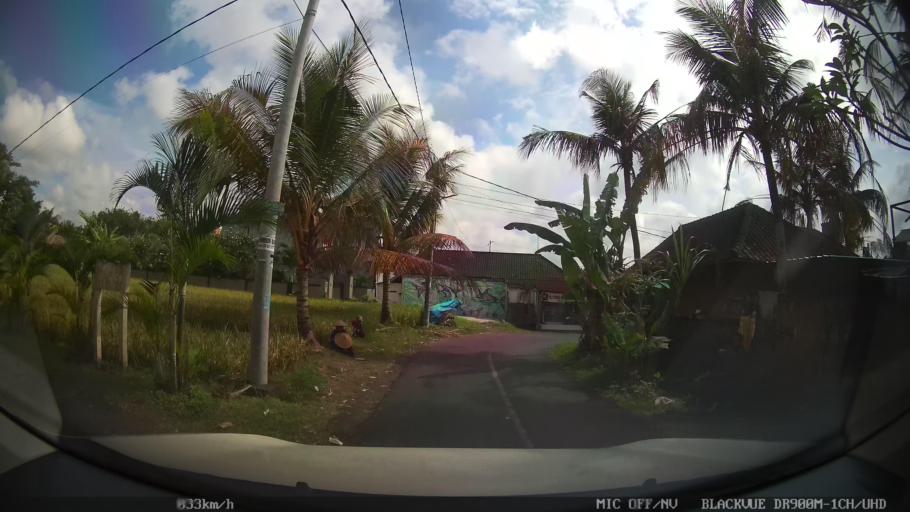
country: ID
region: Bali
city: Banjar Tebongkang
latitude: -8.5402
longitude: 115.2500
